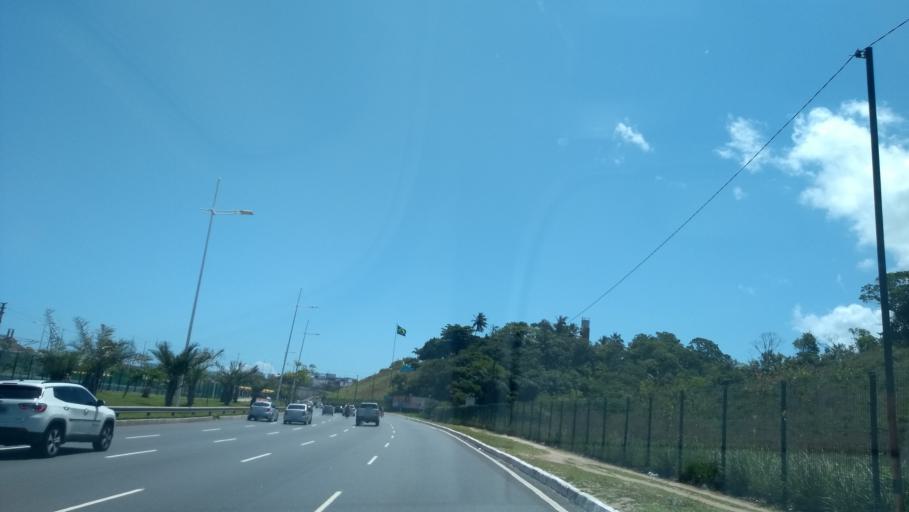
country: BR
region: Bahia
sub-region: Salvador
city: Salvador
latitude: -12.9400
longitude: -38.4173
